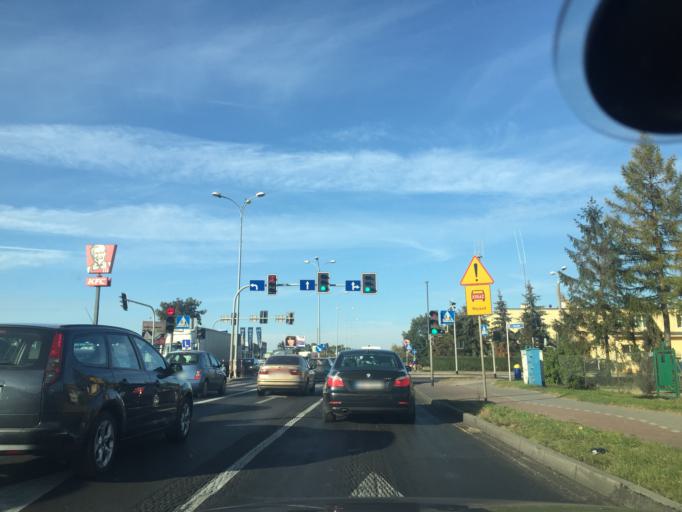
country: PL
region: Kujawsko-Pomorskie
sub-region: Powiat inowroclawski
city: Inowroclaw
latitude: 52.7788
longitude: 18.2598
